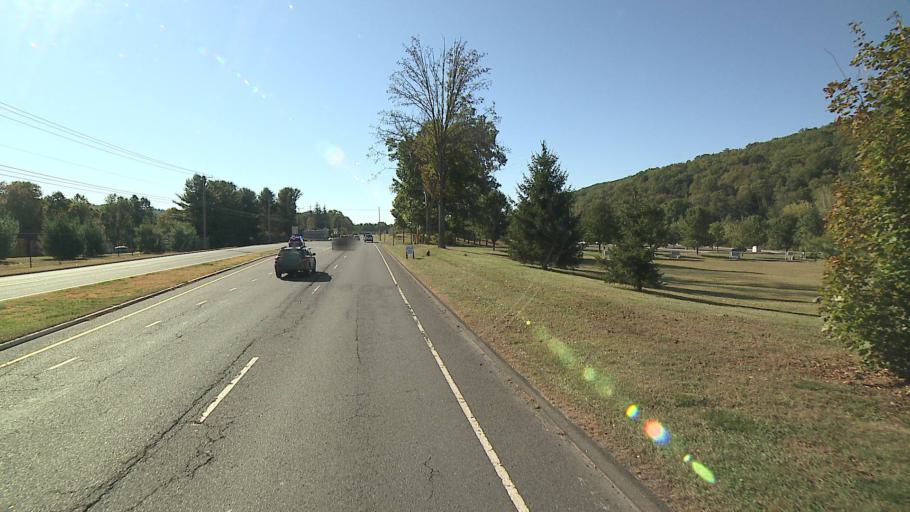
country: US
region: Connecticut
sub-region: Litchfield County
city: New Milford
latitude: 41.5062
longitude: -73.4195
